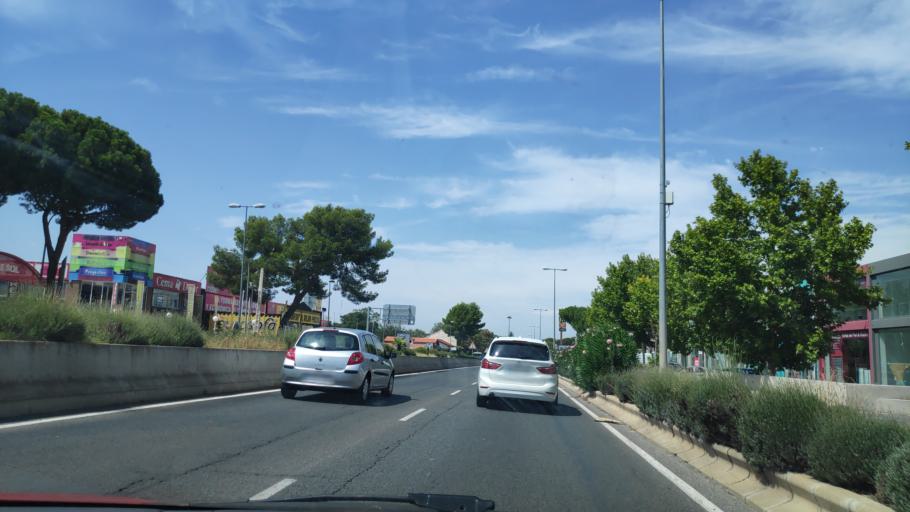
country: ES
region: Madrid
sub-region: Provincia de Madrid
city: Vaciamadrid
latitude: 40.3112
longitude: -3.4847
